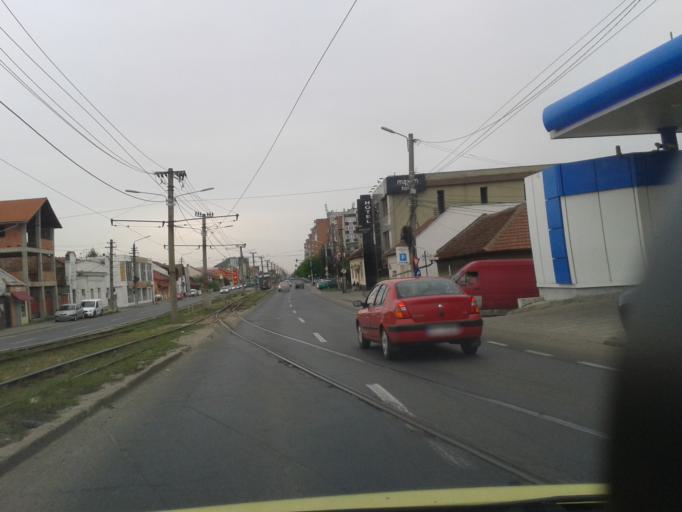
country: RO
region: Arad
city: Arad
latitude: 46.1806
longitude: 21.3417
